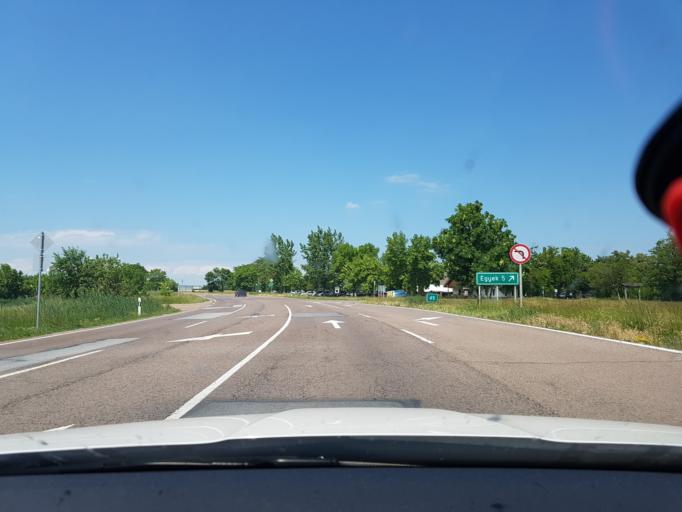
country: HU
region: Hajdu-Bihar
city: Egyek
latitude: 47.5902
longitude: 20.8526
